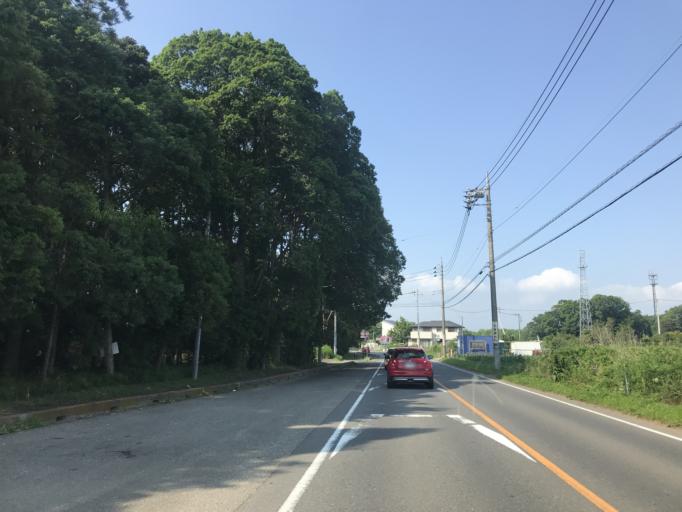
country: JP
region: Ibaraki
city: Naka
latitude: 36.0647
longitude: 140.0943
